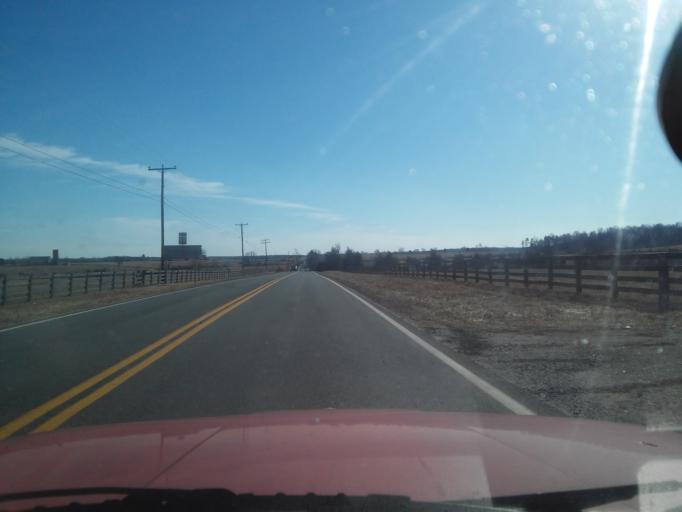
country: US
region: Virginia
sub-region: Orange County
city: Gordonsville
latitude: 38.0495
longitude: -78.1888
